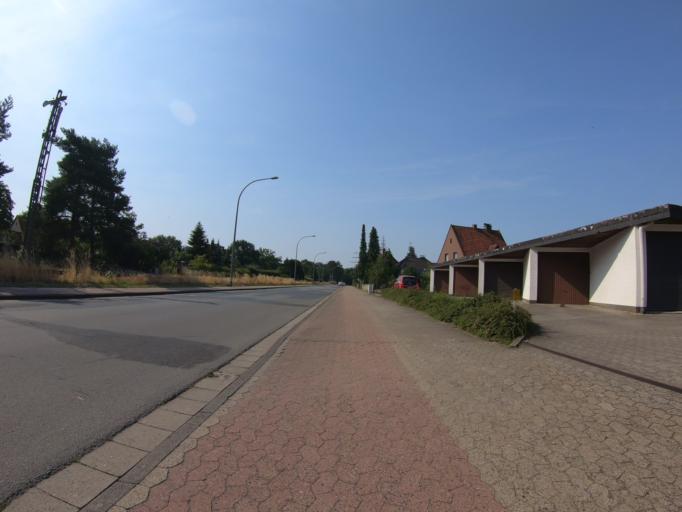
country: DE
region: Lower Saxony
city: Gifhorn
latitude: 52.4750
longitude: 10.5345
